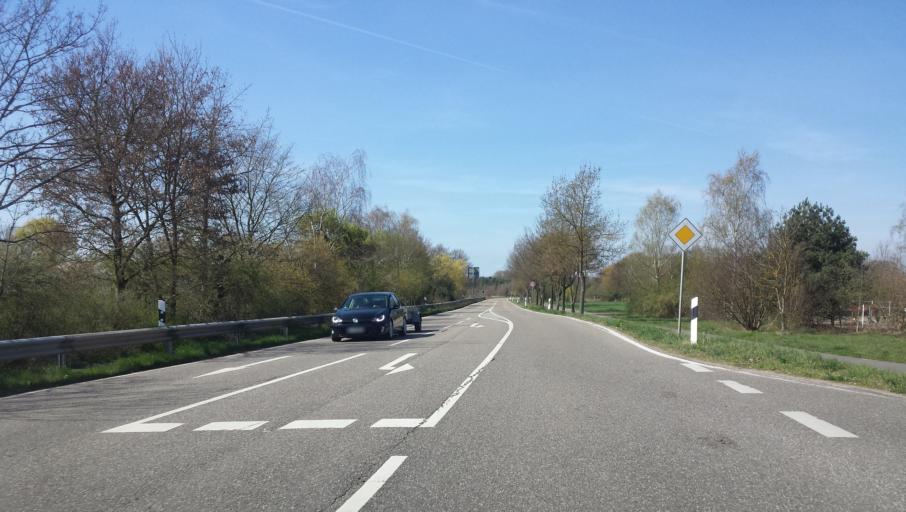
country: DE
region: Rheinland-Pfalz
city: Schifferstadt
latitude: 49.3707
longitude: 8.3660
